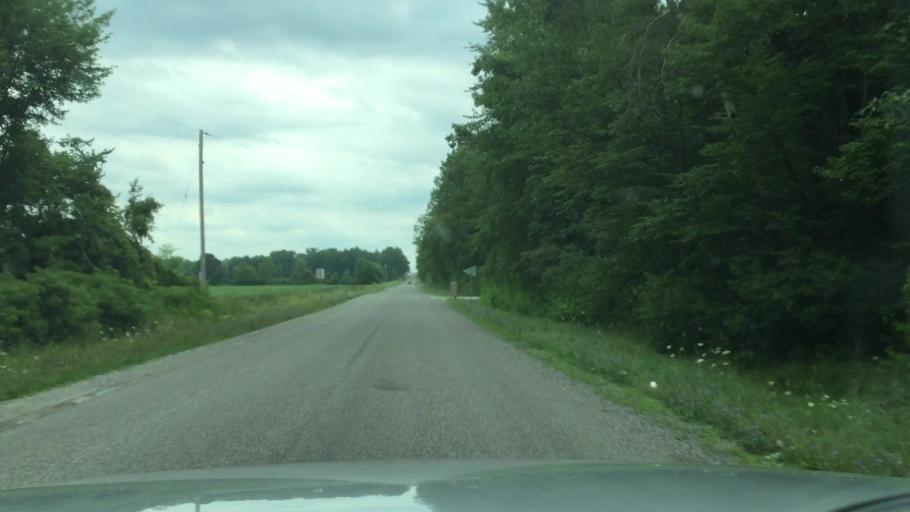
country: US
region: Michigan
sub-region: Saginaw County
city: Bridgeport
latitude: 43.3217
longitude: -83.8608
